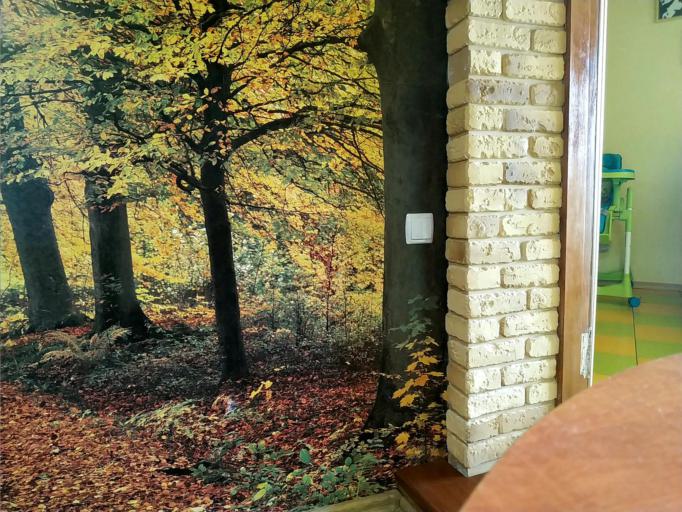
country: RU
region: Smolensk
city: Ozernyy
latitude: 55.4579
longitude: 32.6640
